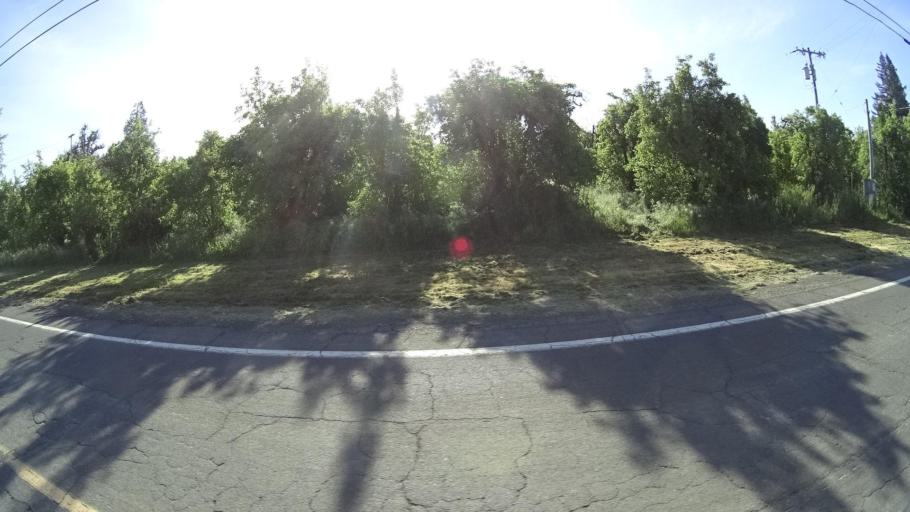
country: US
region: California
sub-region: Lake County
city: Lakeport
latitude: 39.0743
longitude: -122.9498
